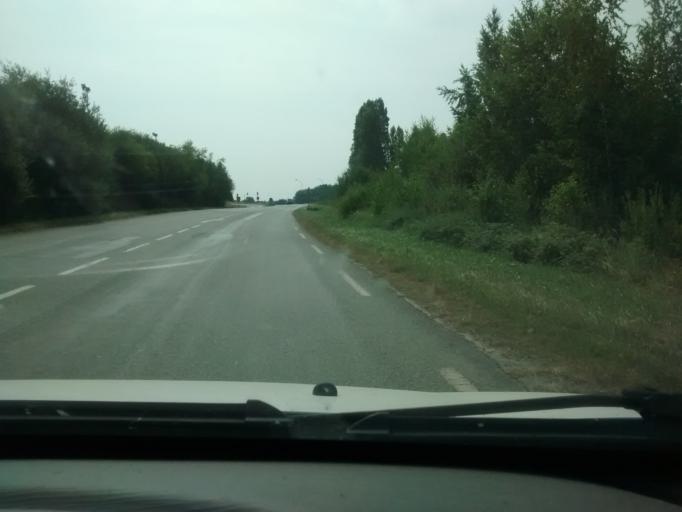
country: FR
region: Brittany
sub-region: Departement d'Ille-et-Vilaine
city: Saint-Jacques-de-la-Lande
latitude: 48.0641
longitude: -1.7030
